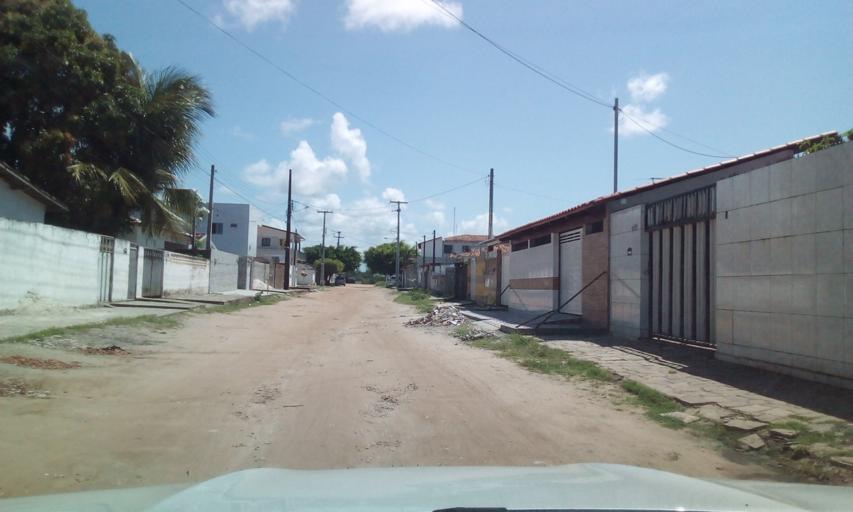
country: BR
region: Paraiba
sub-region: Conde
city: Conde
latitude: -7.2085
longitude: -34.8541
